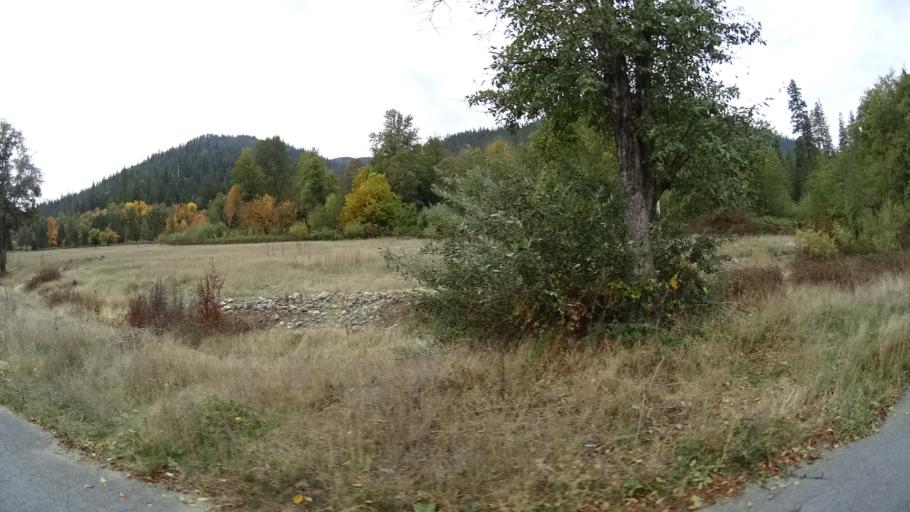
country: US
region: California
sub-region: Siskiyou County
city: Happy Camp
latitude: 41.8406
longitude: -123.2105
